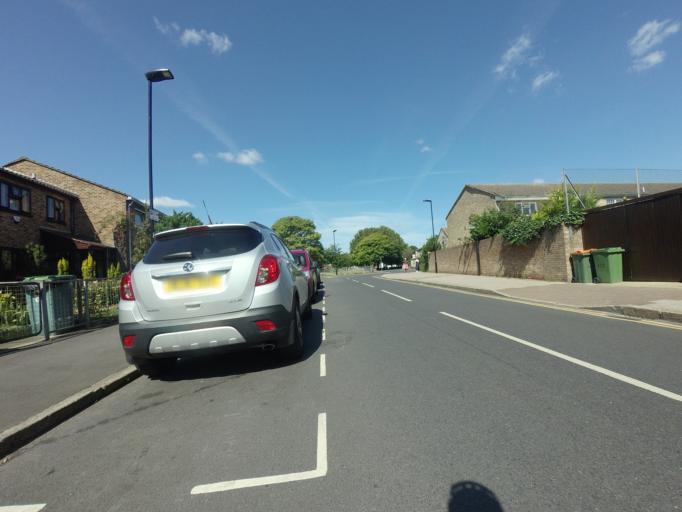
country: GB
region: England
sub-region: Greater London
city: Poplar
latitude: 51.5197
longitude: 0.0102
